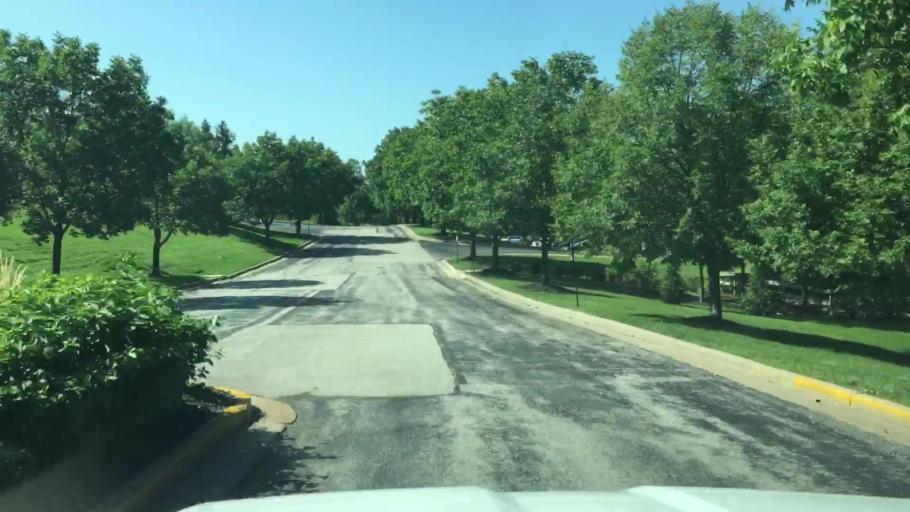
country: US
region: Missouri
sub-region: Saint Louis County
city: Manchester
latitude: 38.6406
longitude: -90.5061
